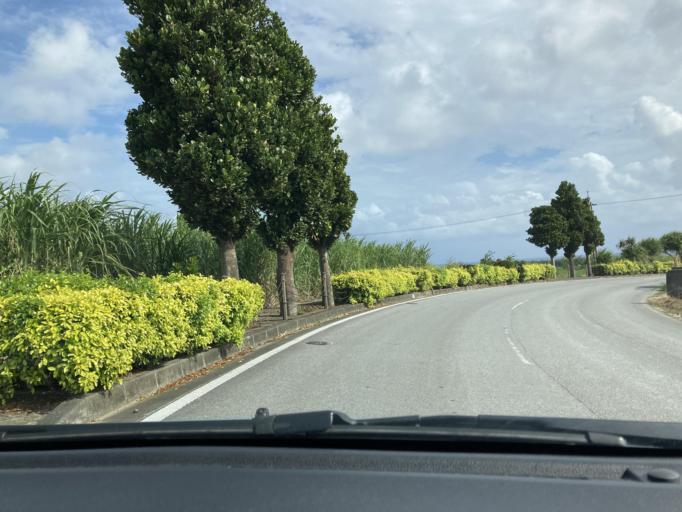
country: JP
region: Okinawa
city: Itoman
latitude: 26.0931
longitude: 127.6938
